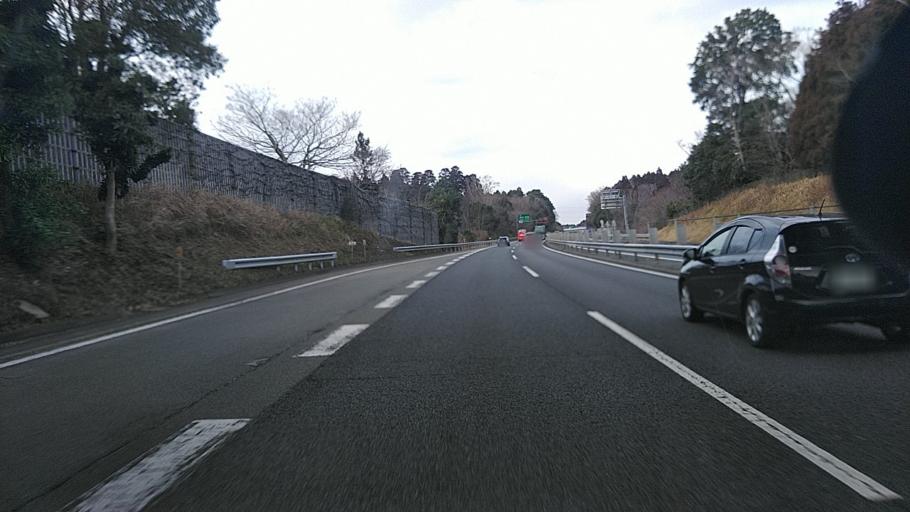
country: JP
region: Chiba
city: Oami
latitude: 35.5697
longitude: 140.2314
